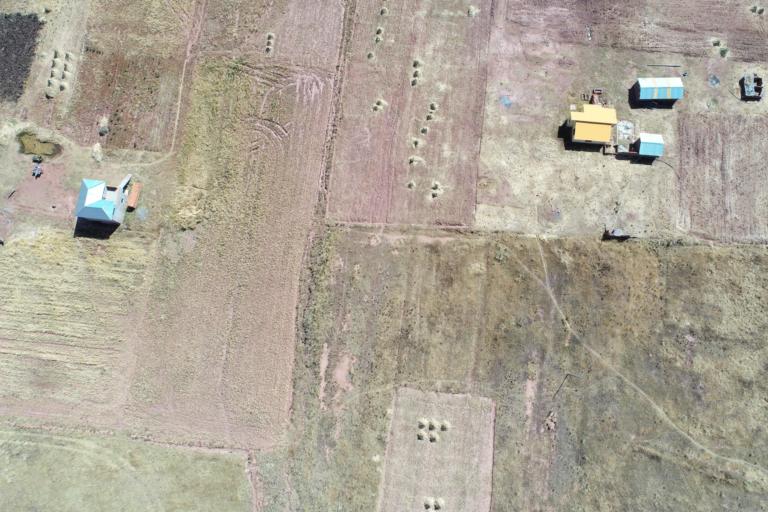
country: BO
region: La Paz
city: Tiahuanaco
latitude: -16.5949
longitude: -68.7547
